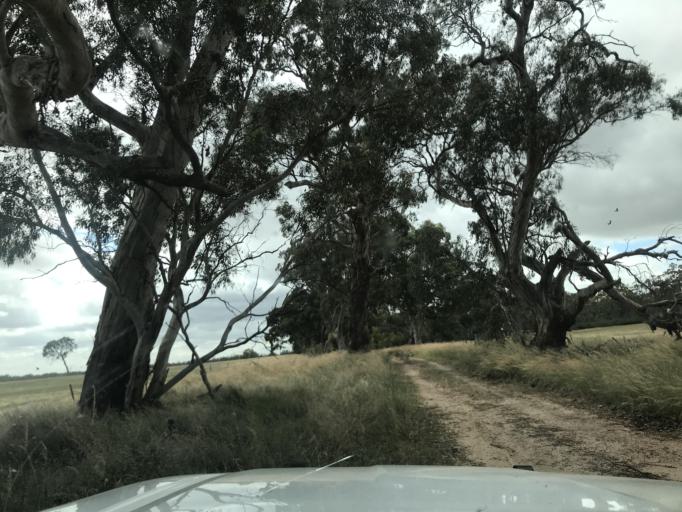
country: AU
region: South Australia
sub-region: Naracoorte and Lucindale
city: Naracoorte
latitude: -36.9021
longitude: 141.4173
